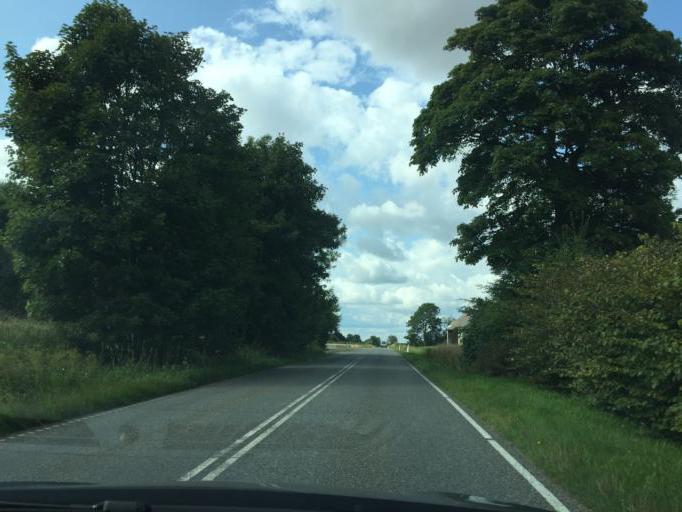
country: DK
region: South Denmark
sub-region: Vejle Kommune
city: Jelling
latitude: 55.7841
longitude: 9.4833
